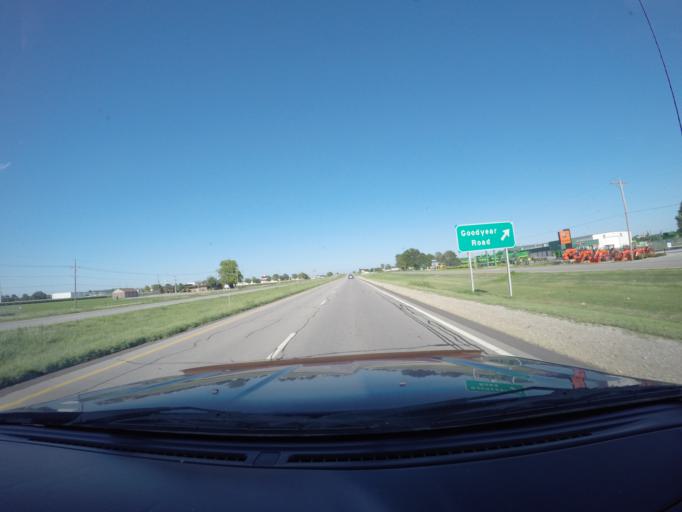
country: US
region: Kansas
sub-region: Shawnee County
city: Topeka
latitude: 39.0907
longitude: -95.7040
